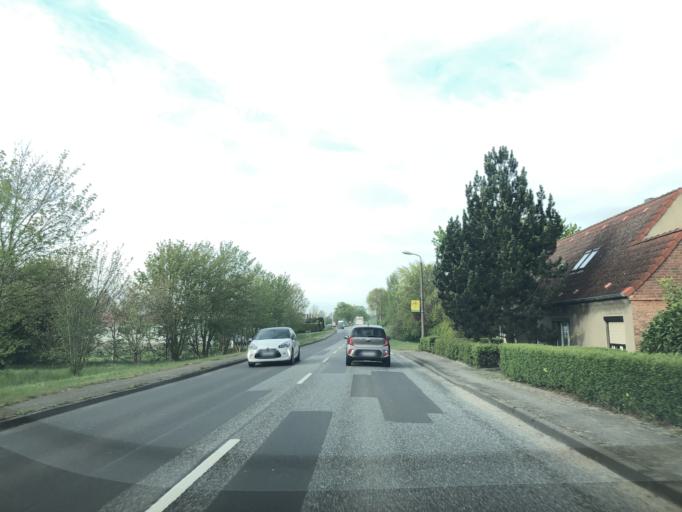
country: DE
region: Mecklenburg-Vorpommern
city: Laage
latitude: 53.8842
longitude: 12.2490
